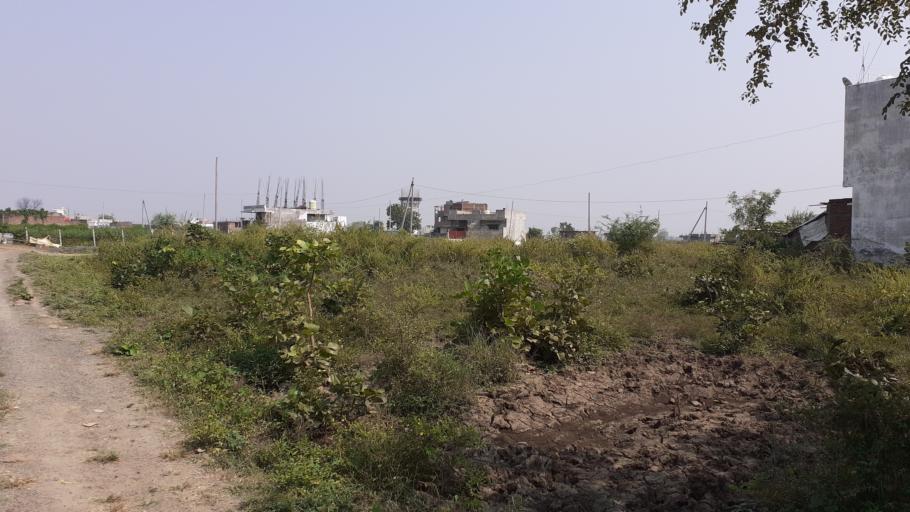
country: IN
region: Maharashtra
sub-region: Nagpur Division
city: Nagpur
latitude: 21.1119
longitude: 79.1596
